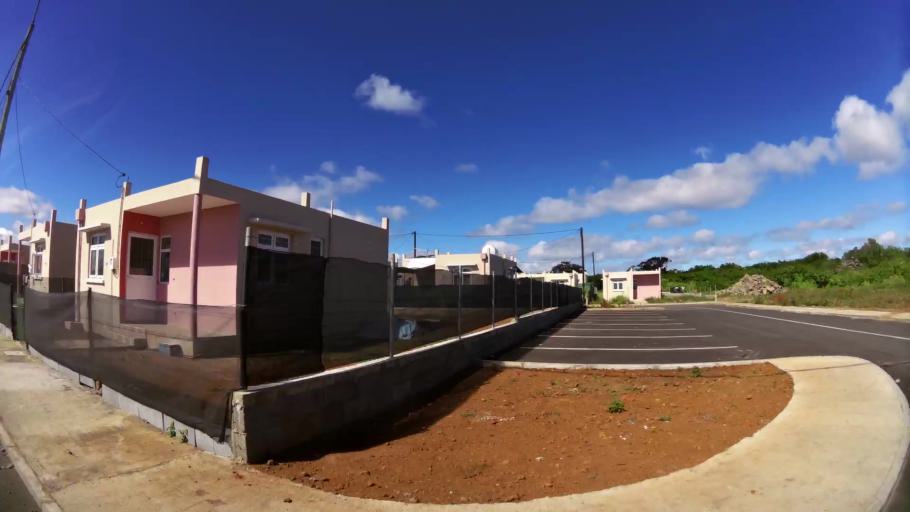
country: MU
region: Plaines Wilhems
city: Vacoas
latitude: -20.3289
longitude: 57.4812
